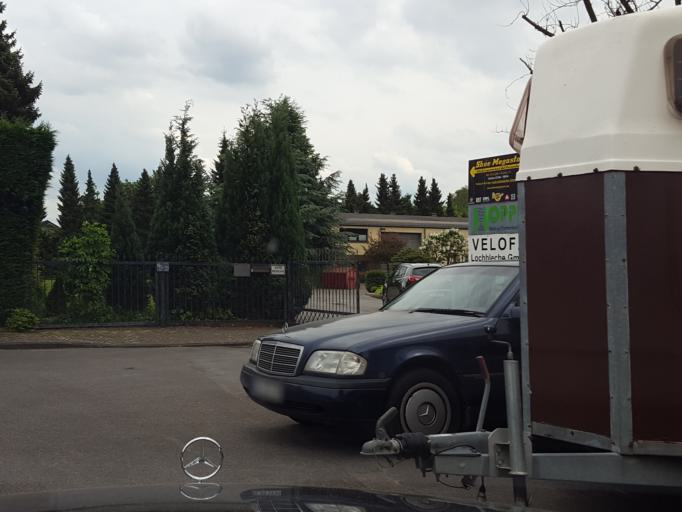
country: DE
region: North Rhine-Westphalia
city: Oer-Erkenschwick
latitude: 51.6465
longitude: 7.2822
